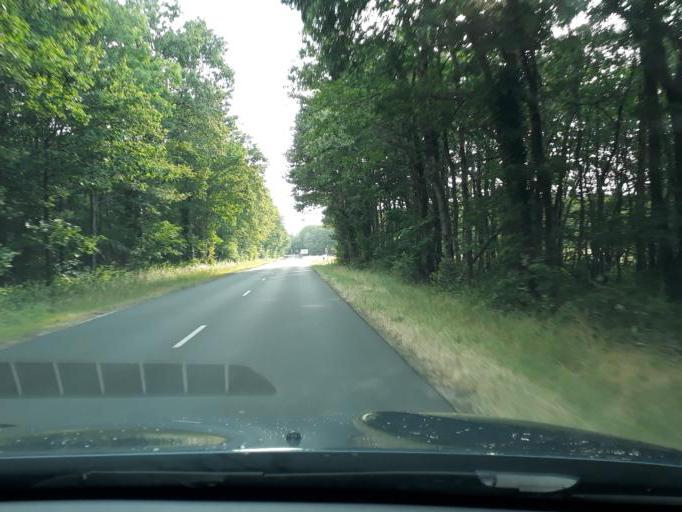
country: FR
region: Centre
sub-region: Departement du Loiret
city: Saint-Cyr-en-Val
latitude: 47.8206
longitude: 1.9592
